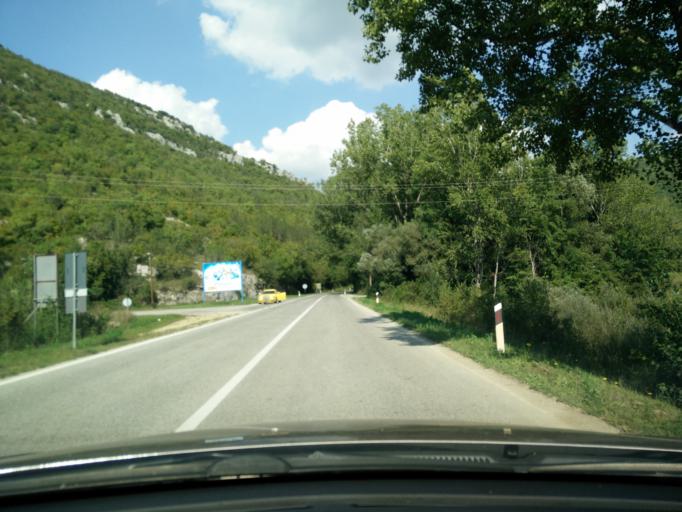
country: HR
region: Istarska
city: Buzet
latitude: 45.3784
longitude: 13.8901
